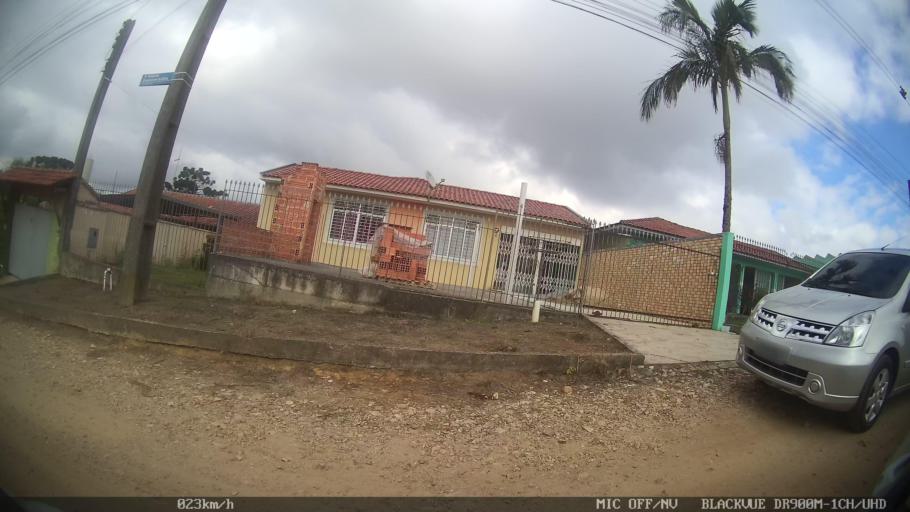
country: BR
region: Parana
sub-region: Colombo
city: Colombo
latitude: -25.3562
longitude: -49.2332
